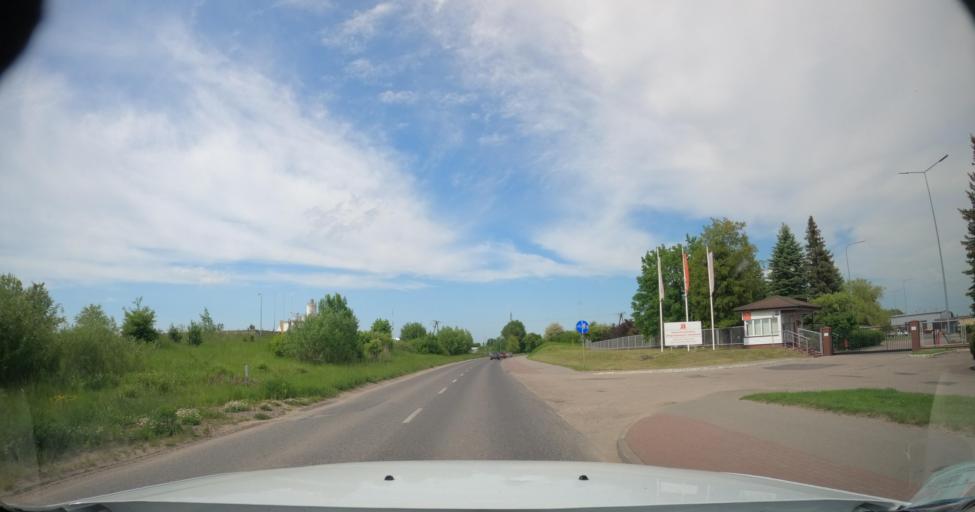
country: PL
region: Warmian-Masurian Voivodeship
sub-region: Powiat lidzbarski
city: Lidzbark Warminski
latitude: 54.1334
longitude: 20.5655
